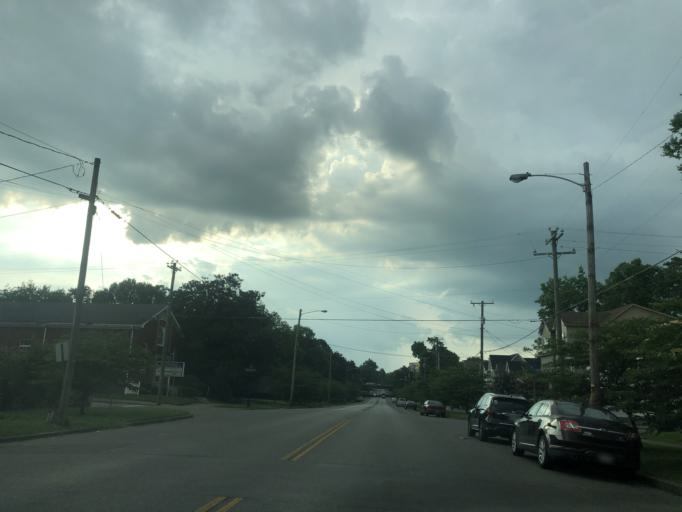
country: US
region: Tennessee
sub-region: Davidson County
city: Nashville
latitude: 36.1751
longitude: -86.7979
